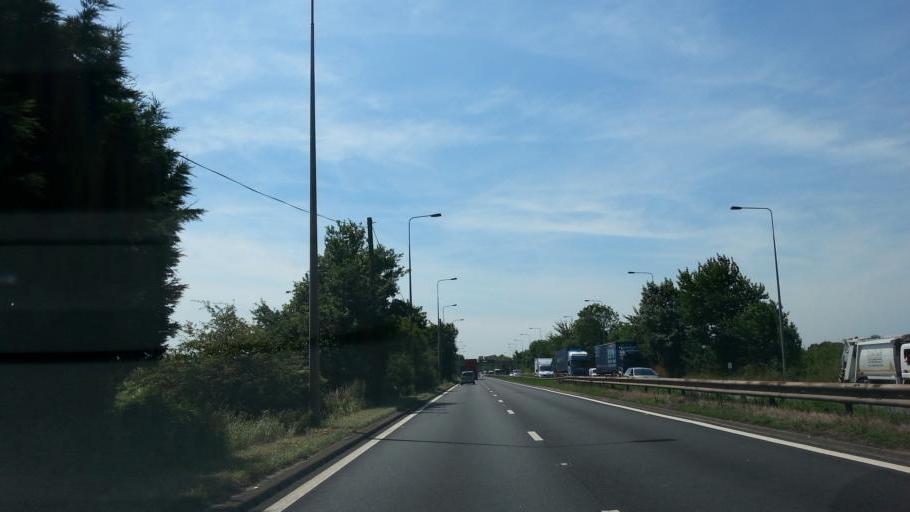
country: GB
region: England
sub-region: Staffordshire
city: Alrewas
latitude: 52.7190
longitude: -1.7560
